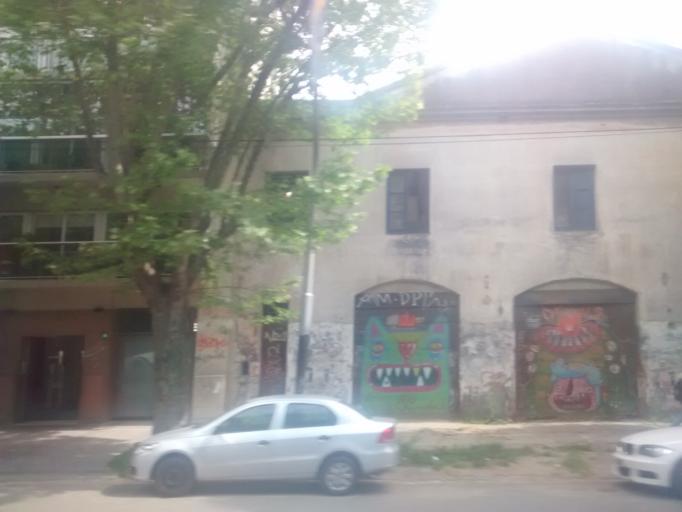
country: AR
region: Buenos Aires
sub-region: Partido de La Plata
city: La Plata
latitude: -34.9126
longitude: -57.9392
